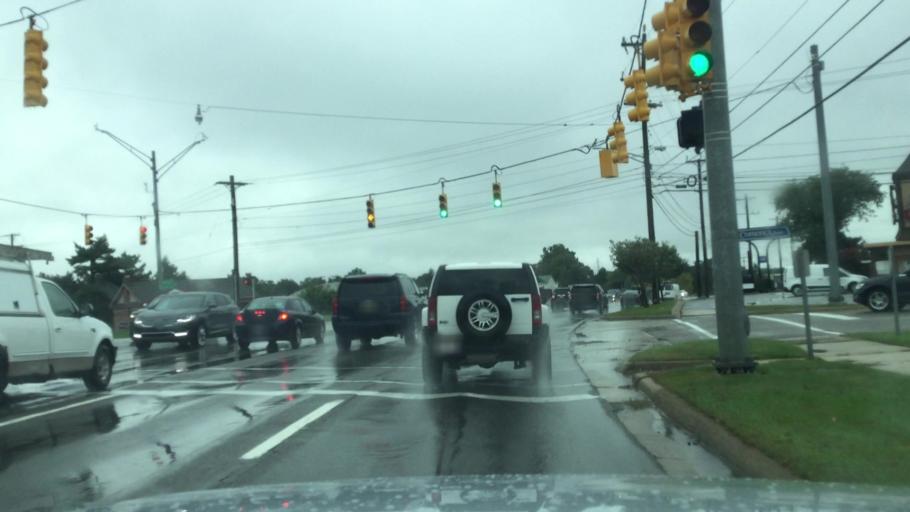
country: US
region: Michigan
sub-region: Oakland County
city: Sylvan Lake
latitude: 42.6115
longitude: -83.3284
